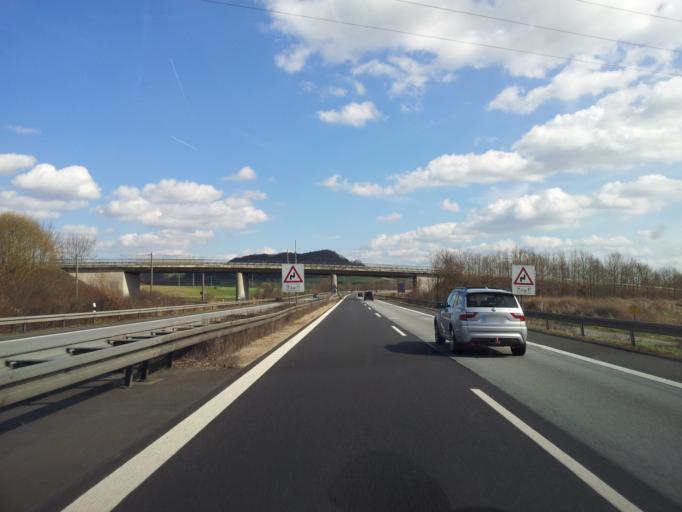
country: DE
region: Bavaria
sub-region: Regierungsbezirk Unterfranken
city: Stettfeld
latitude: 49.9665
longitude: 10.7195
